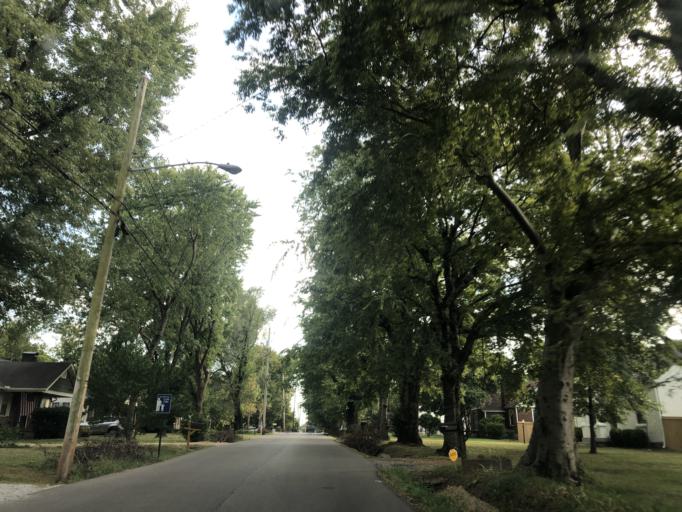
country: US
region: Tennessee
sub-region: Davidson County
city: Oak Hill
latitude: 36.1041
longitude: -86.7346
